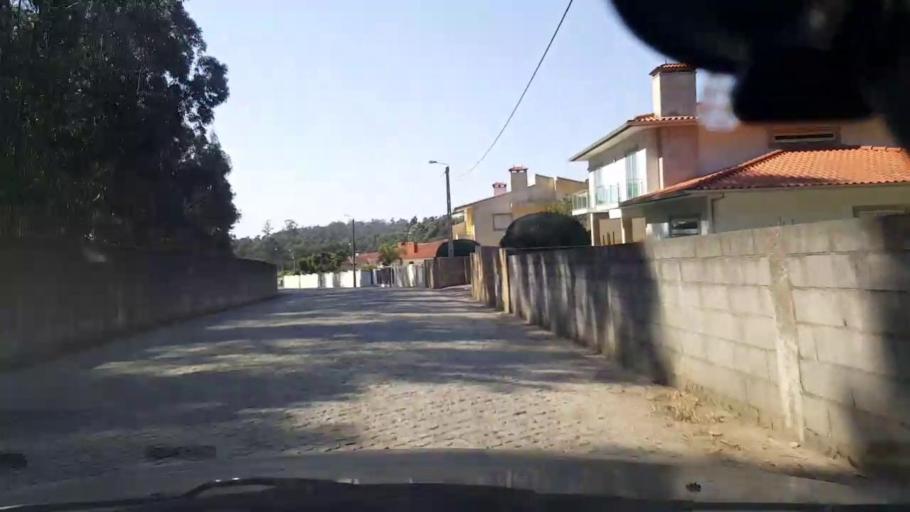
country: PT
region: Porto
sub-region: Povoa de Varzim
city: Pedroso
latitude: 41.4035
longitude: -8.7052
